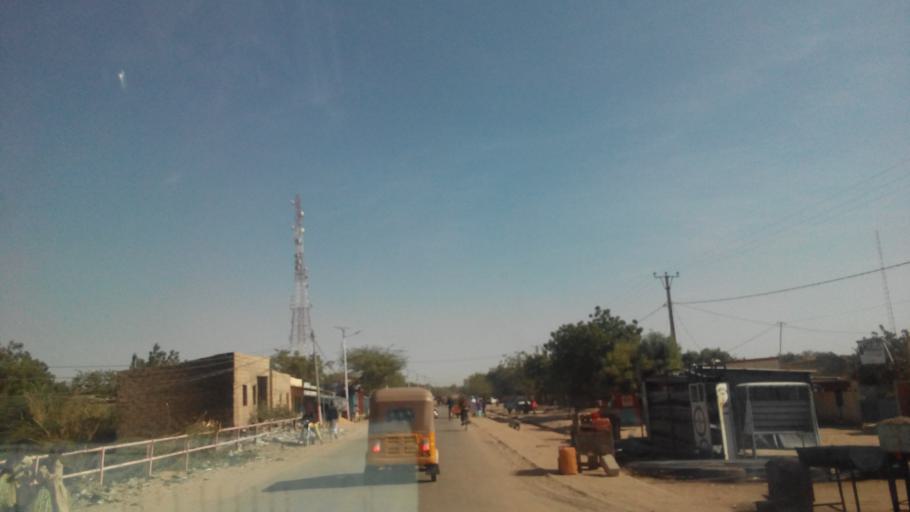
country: NE
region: Maradi
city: Tessaoua
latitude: 13.7516
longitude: 7.9891
